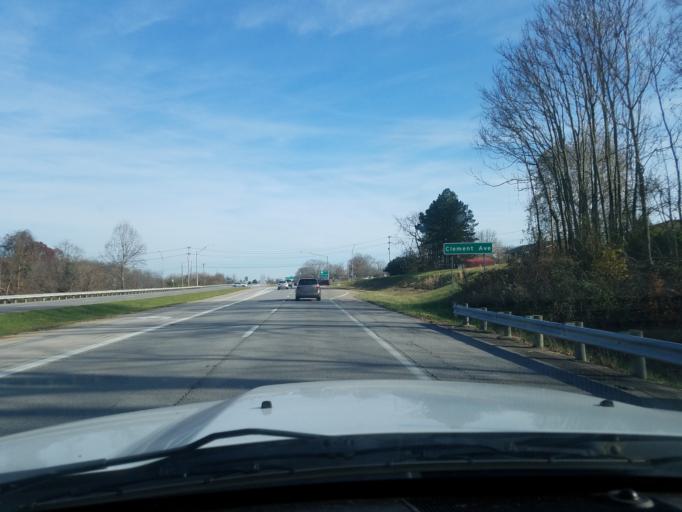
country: US
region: Ohio
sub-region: Washington County
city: Belpre
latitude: 39.2842
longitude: -81.5807
